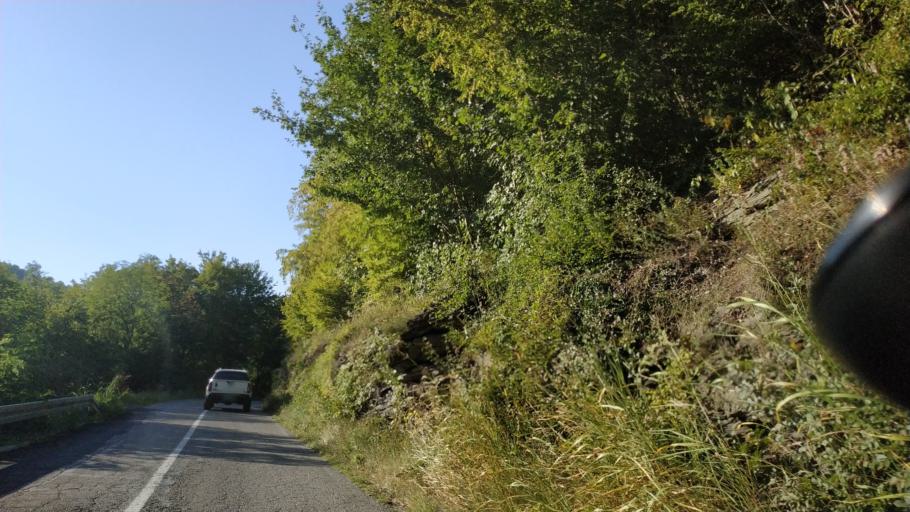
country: RS
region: Central Serbia
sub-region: Rasinski Okrug
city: Krusevac
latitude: 43.4630
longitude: 21.3606
